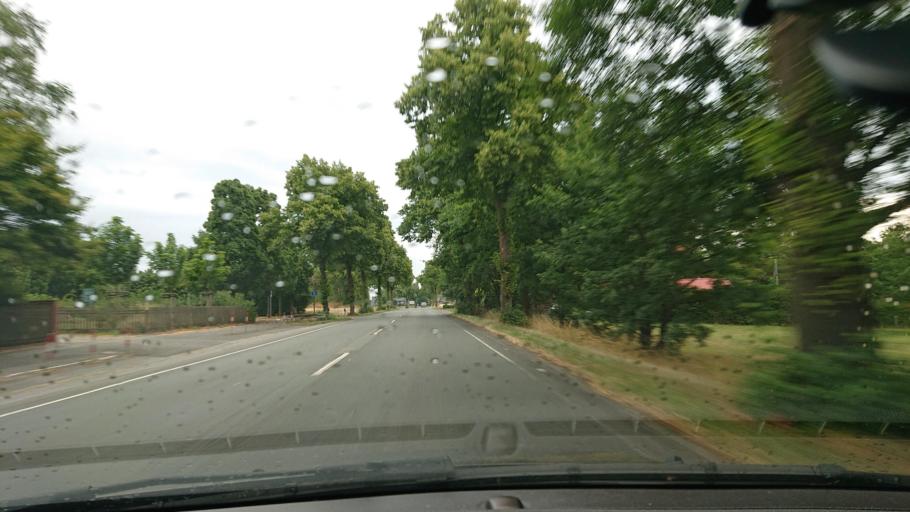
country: DE
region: North Rhine-Westphalia
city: Ahlen
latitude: 51.7075
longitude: 7.9269
